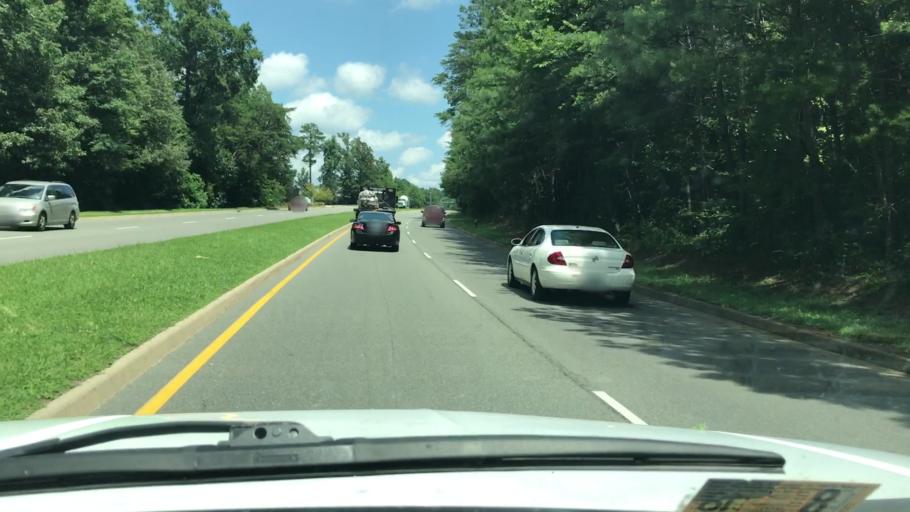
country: US
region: Virginia
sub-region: Henrico County
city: Short Pump
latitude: 37.6278
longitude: -77.5810
